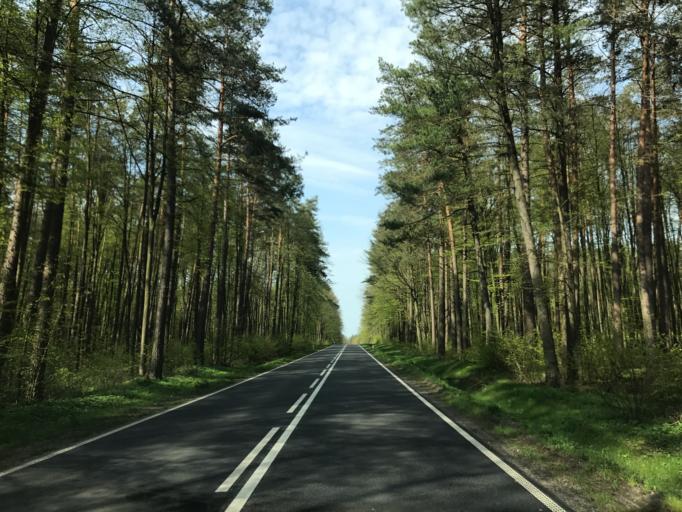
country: PL
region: Warmian-Masurian Voivodeship
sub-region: Powiat dzialdowski
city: Lidzbark
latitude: 53.3278
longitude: 19.8169
